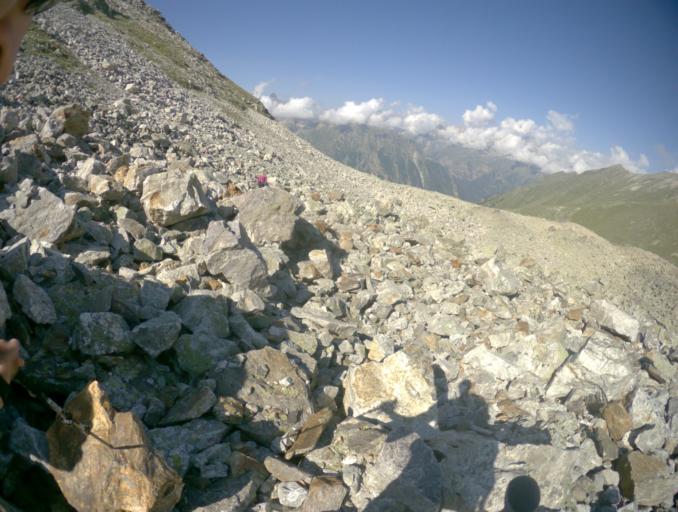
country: RU
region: Karachayevo-Cherkesiya
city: Uchkulan
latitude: 43.3074
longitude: 42.0658
